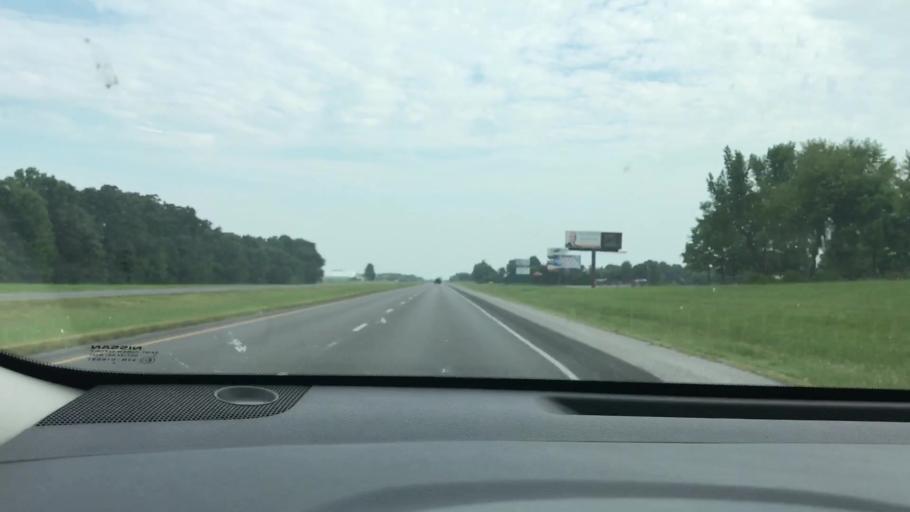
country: US
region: Kentucky
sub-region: Calloway County
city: Murray
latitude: 36.6836
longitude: -88.3027
